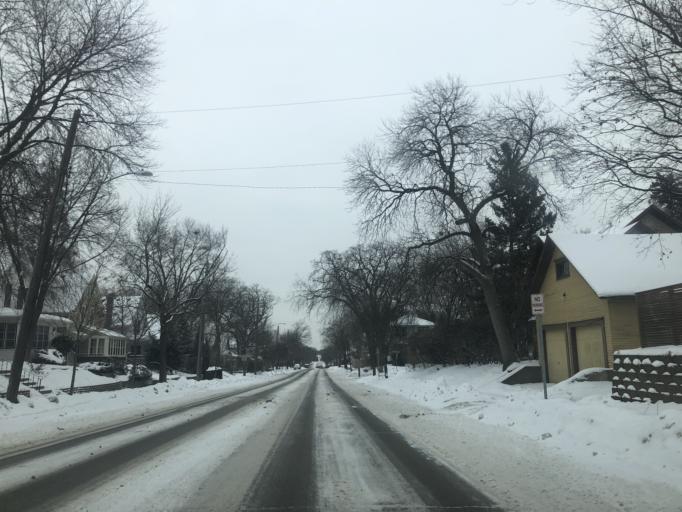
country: US
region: Minnesota
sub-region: Hennepin County
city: Richfield
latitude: 44.9304
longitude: -93.2827
